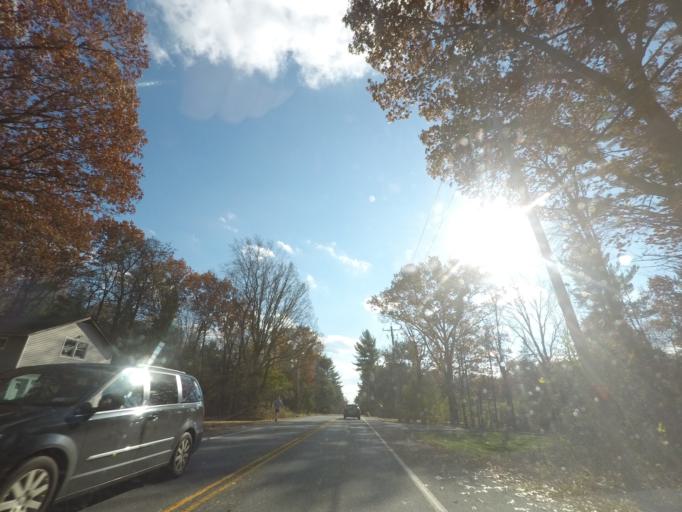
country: US
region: New York
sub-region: Schenectady County
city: East Glenville
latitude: 42.8737
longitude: -73.8876
